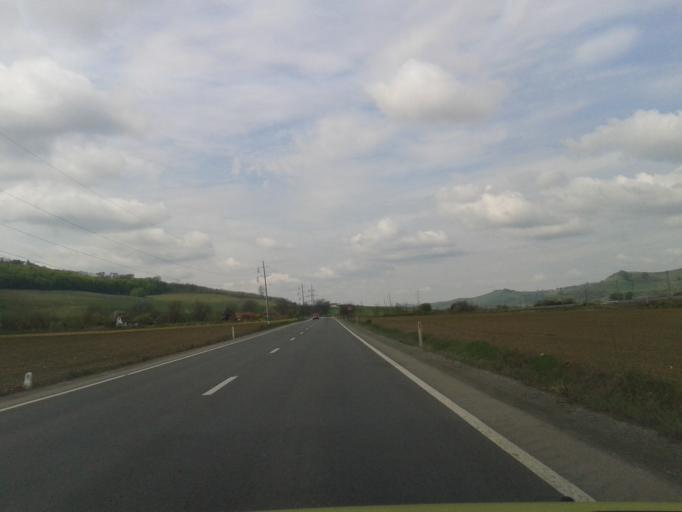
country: RO
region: Sibiu
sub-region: Comuna Alma
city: Alma
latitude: 46.2040
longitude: 24.5065
